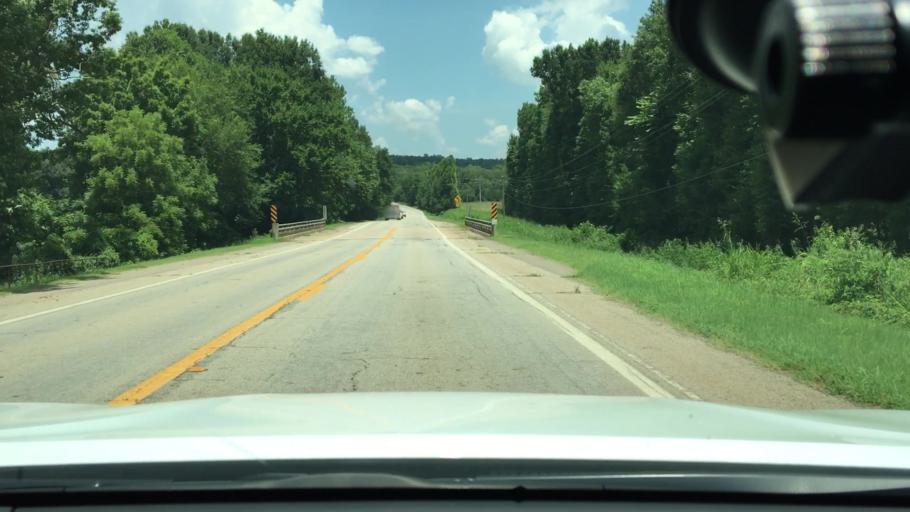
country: US
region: Arkansas
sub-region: Logan County
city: Booneville
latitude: 35.2044
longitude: -93.9243
